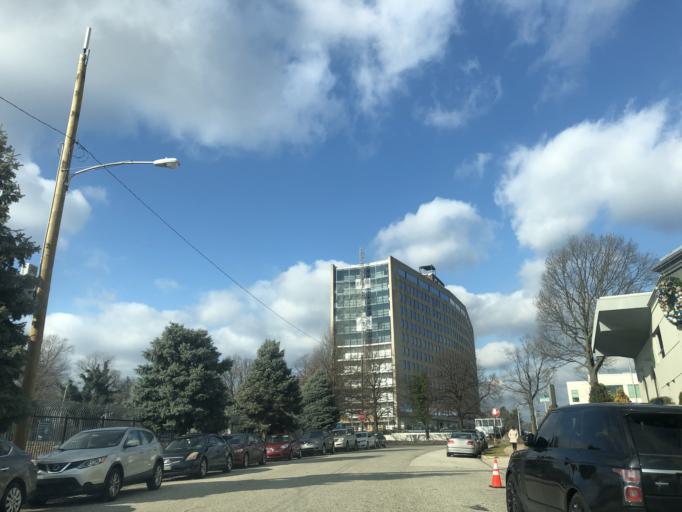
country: US
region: Pennsylvania
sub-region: Montgomery County
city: Bala-Cynwyd
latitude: 40.0041
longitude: -75.2186
